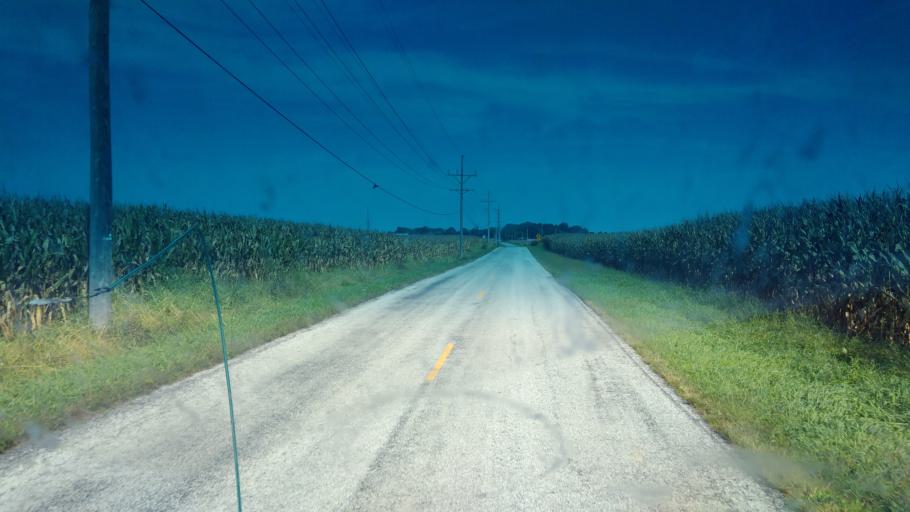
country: US
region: Ohio
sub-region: Marion County
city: Marion
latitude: 40.6705
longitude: -83.2120
